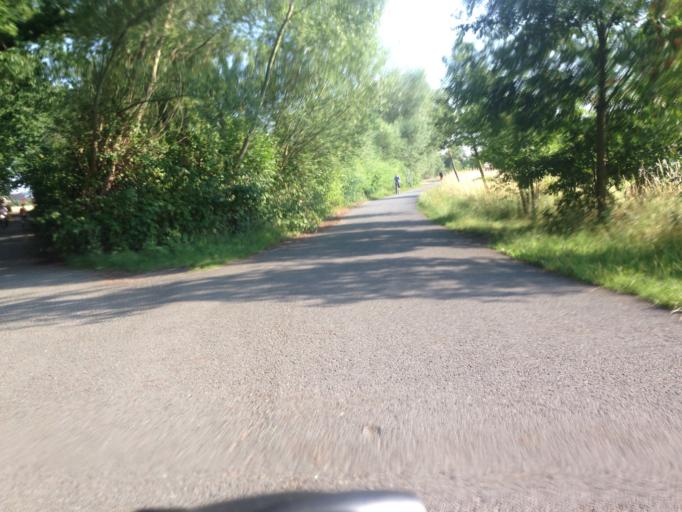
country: DE
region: North Rhine-Westphalia
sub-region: Regierungsbezirk Munster
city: Muenster
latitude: 51.9792
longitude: 7.6067
